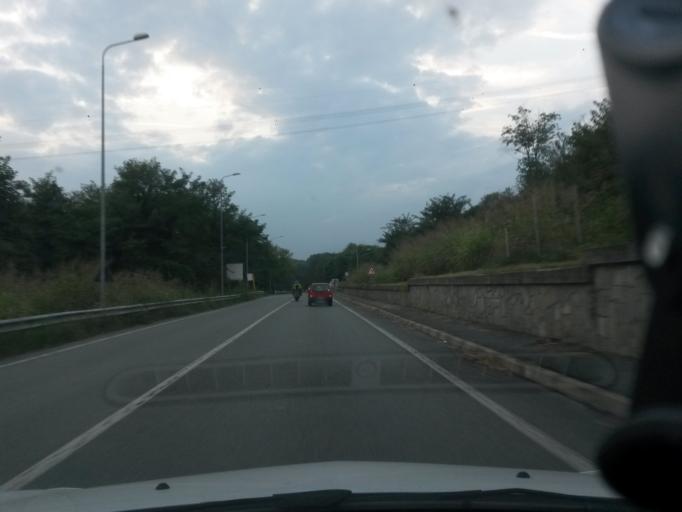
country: IT
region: Piedmont
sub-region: Provincia di Torino
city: Caselette
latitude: 45.0965
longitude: 7.4623
